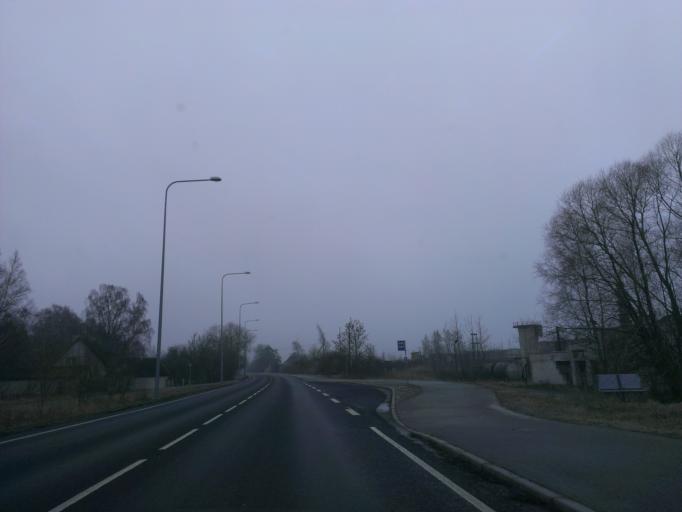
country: EE
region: Laeaene
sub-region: Lihula vald
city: Lihula
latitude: 58.5819
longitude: 23.5247
